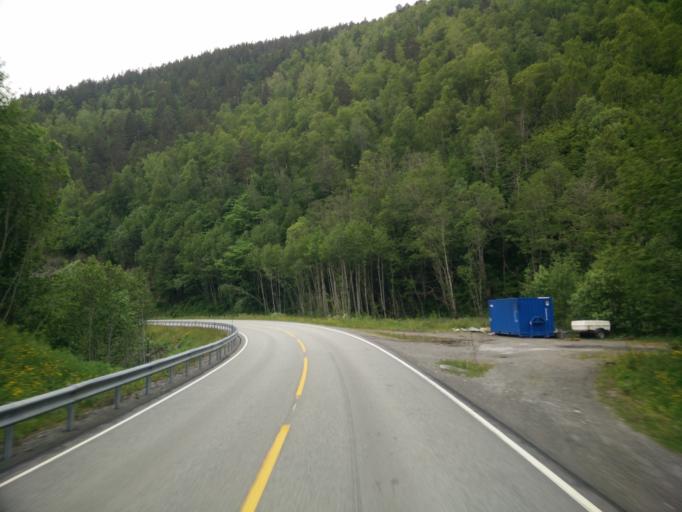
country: NO
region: Sor-Trondelag
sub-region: Hemne
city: Kyrksaeterora
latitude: 63.2148
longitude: 9.1214
